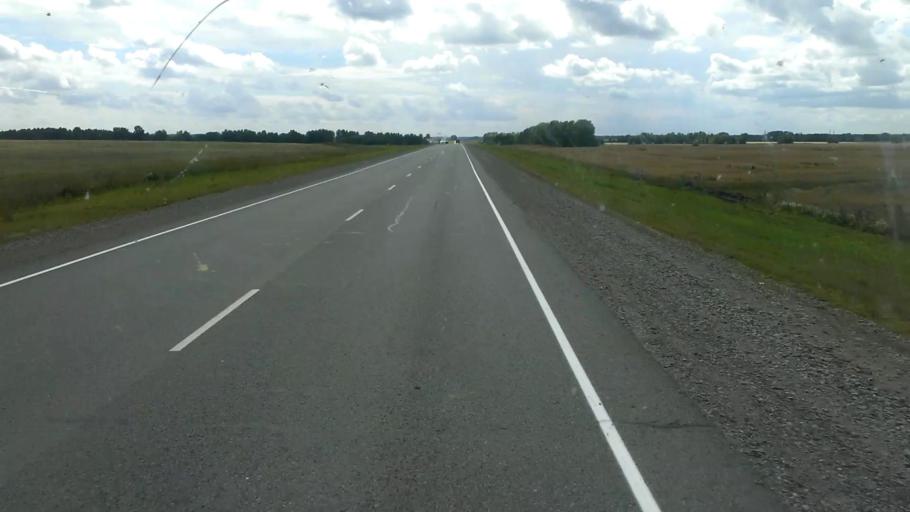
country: RU
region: Altai Krai
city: Troitskoye
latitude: 52.8976
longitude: 84.8338
